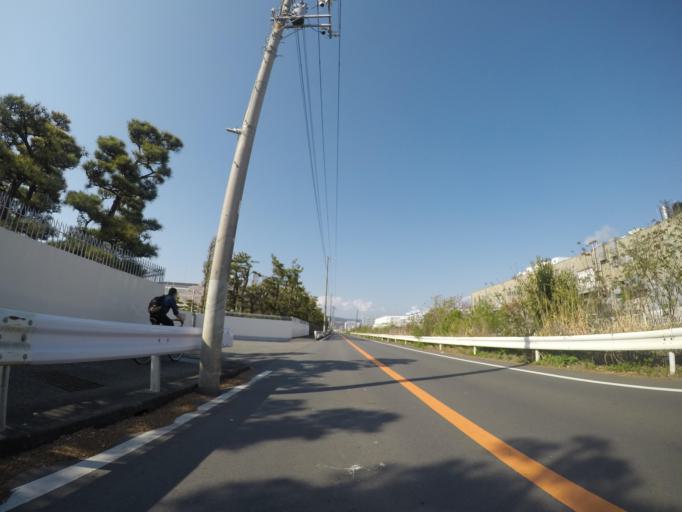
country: JP
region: Shizuoka
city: Numazu
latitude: 35.1062
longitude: 138.8480
